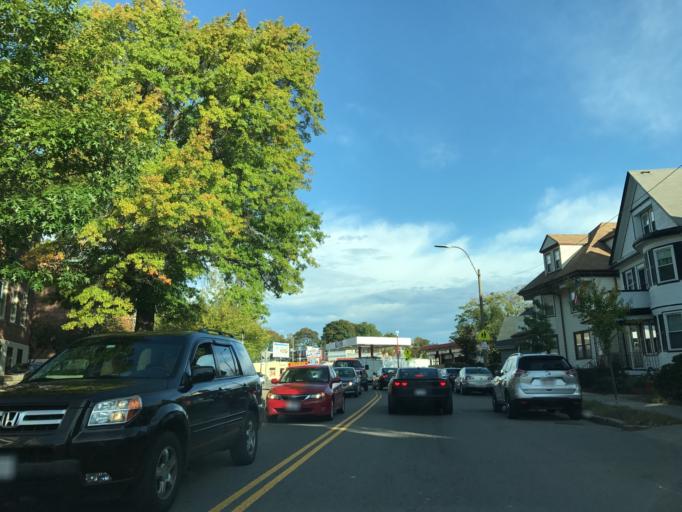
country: US
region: Massachusetts
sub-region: Suffolk County
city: South Boston
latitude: 42.3134
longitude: -71.0592
